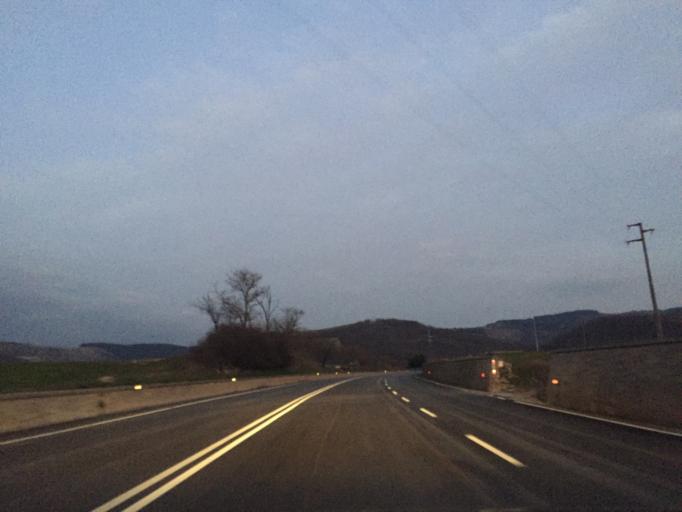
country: IT
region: Apulia
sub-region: Provincia di Foggia
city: Volturara Appula
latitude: 41.4567
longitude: 15.0779
